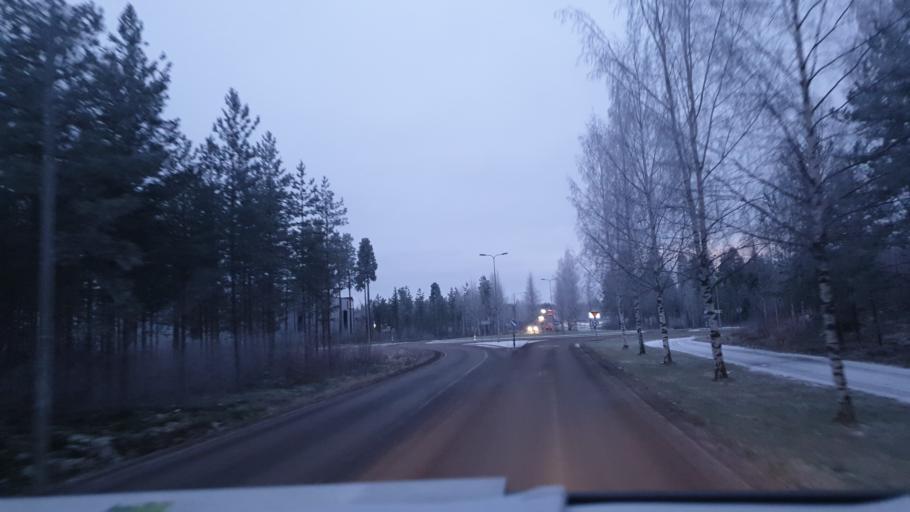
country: FI
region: Southern Ostrobothnia
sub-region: Seinaejoki
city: Nurmo
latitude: 62.7784
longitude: 22.8952
